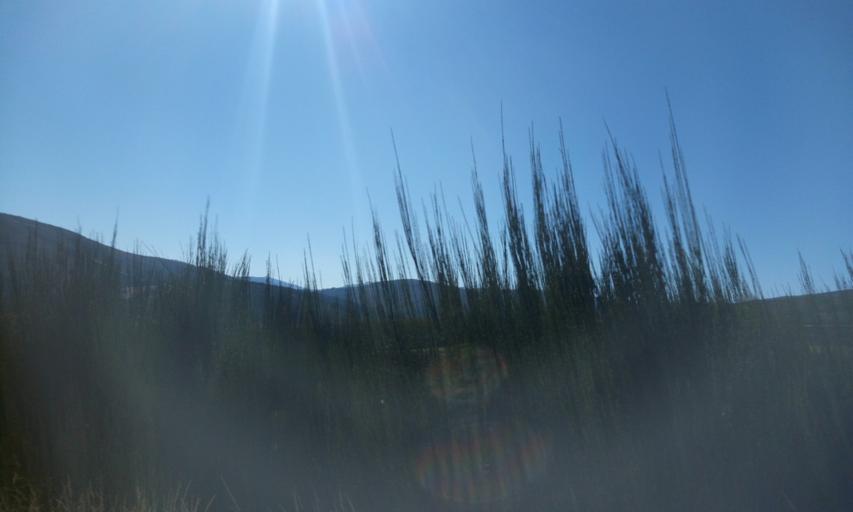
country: PT
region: Guarda
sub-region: Manteigas
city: Manteigas
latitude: 40.4619
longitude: -7.4983
